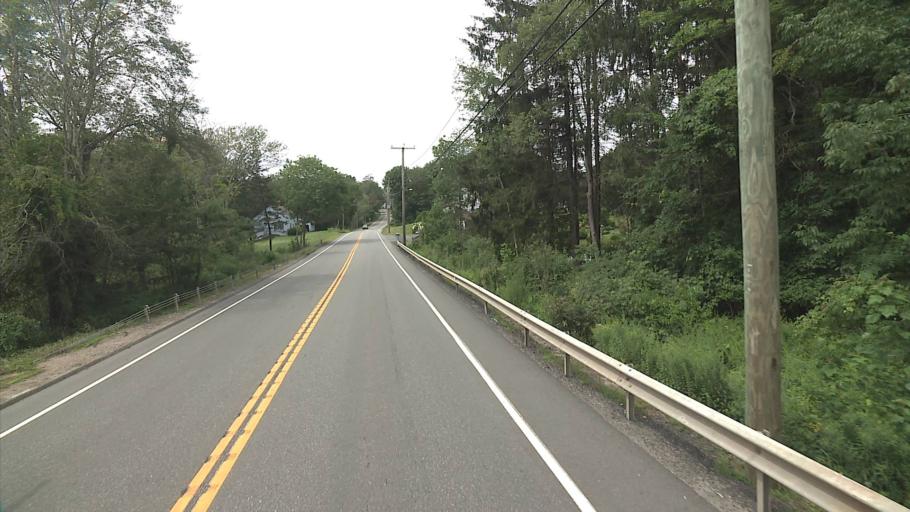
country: US
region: Connecticut
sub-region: Tolland County
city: Stafford Springs
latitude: 41.8795
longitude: -72.2832
